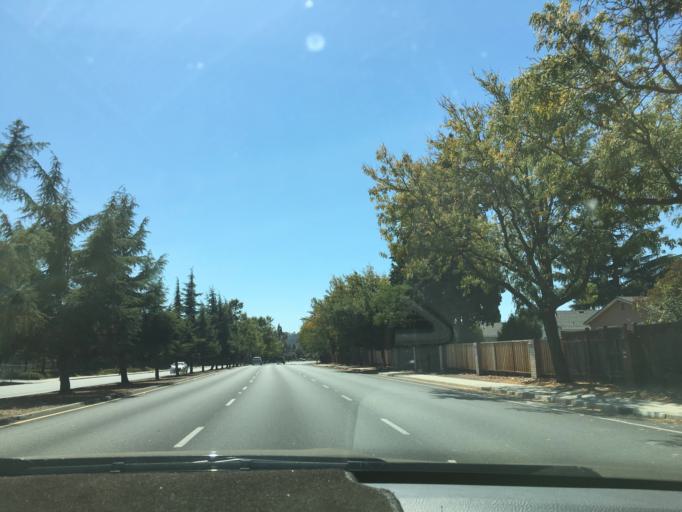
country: US
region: California
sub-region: Santa Clara County
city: Seven Trees
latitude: 37.2375
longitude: -121.8270
